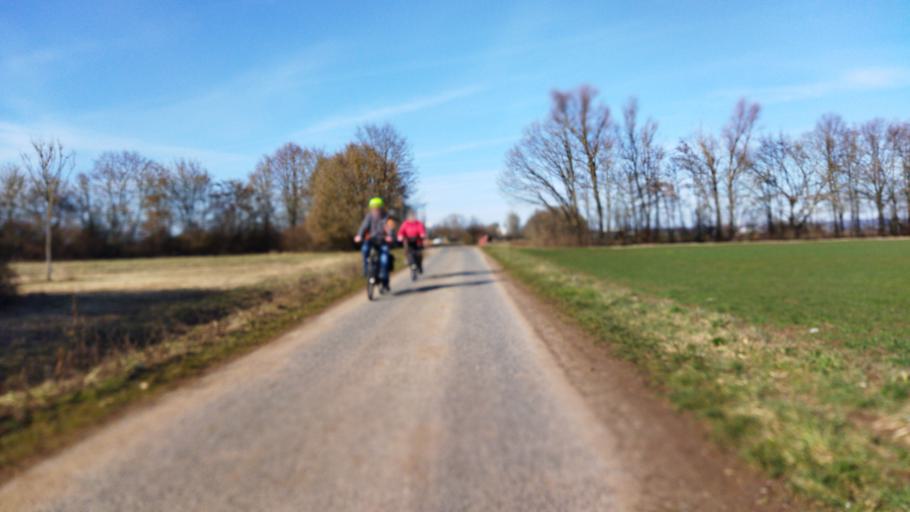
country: DE
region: Bavaria
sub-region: Regierungsbezirk Unterfranken
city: Grafenrheinfeld
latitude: 49.9846
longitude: 10.1995
